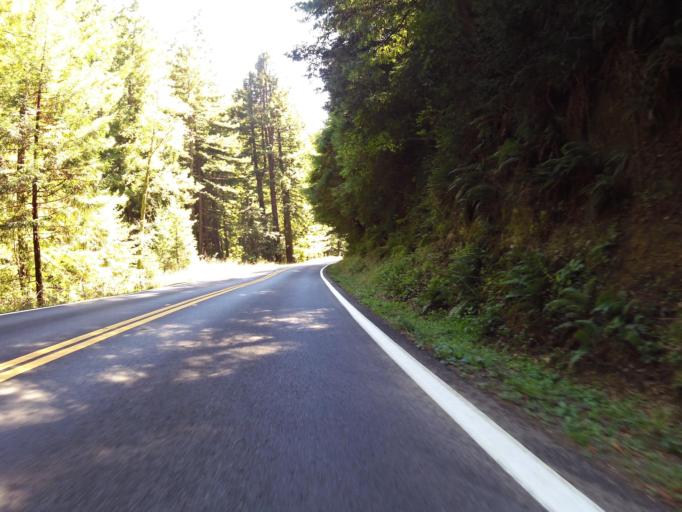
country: US
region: California
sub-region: Mendocino County
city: Fort Bragg
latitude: 39.7213
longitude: -123.8017
